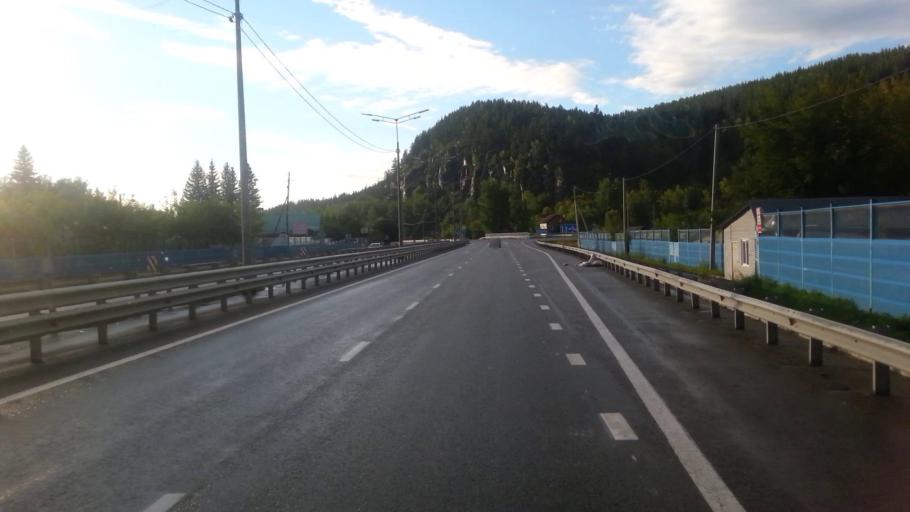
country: RU
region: Altay
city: Souzga
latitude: 51.9166
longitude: 85.8607
